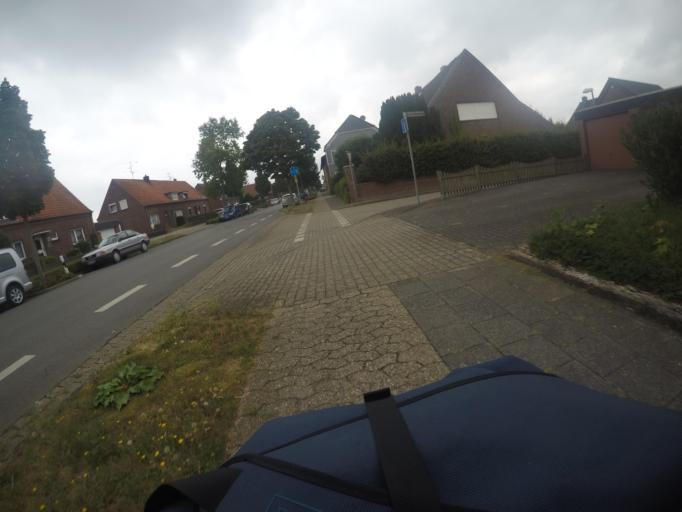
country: DE
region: North Rhine-Westphalia
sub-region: Regierungsbezirk Dusseldorf
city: Kevelaer
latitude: 51.5895
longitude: 6.2395
